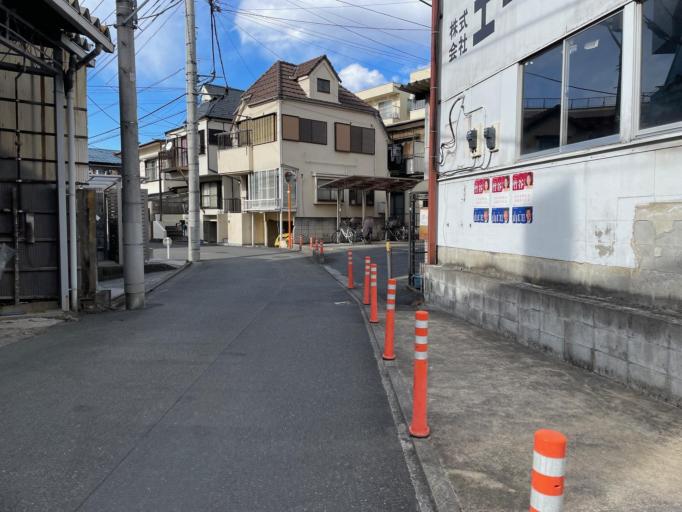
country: JP
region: Tokyo
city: Chofugaoka
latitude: 35.6508
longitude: 139.5314
